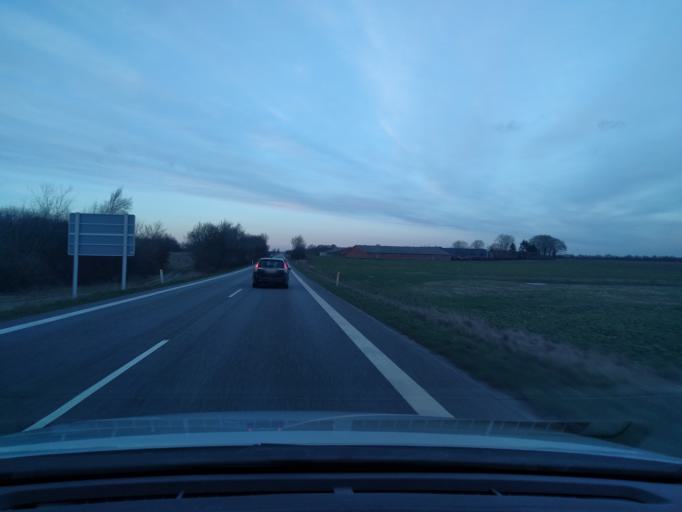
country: DK
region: South Denmark
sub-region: Tonder Kommune
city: Toftlund
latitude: 55.1951
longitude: 9.0792
